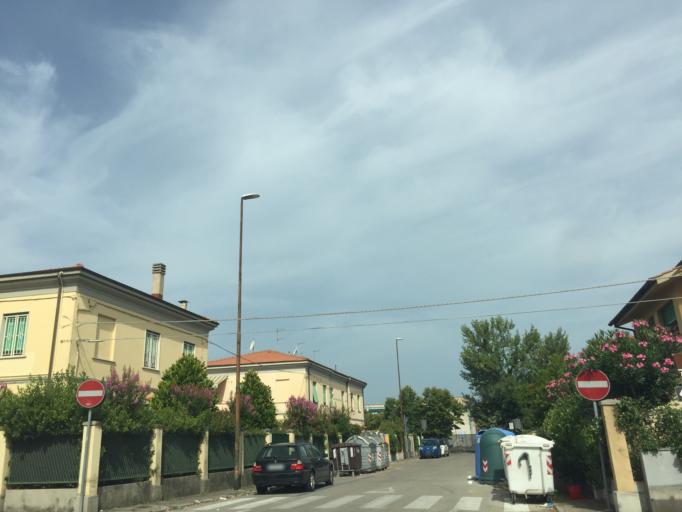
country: IT
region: Tuscany
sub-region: Province of Pisa
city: Pisa
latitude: 43.7203
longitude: 10.3860
